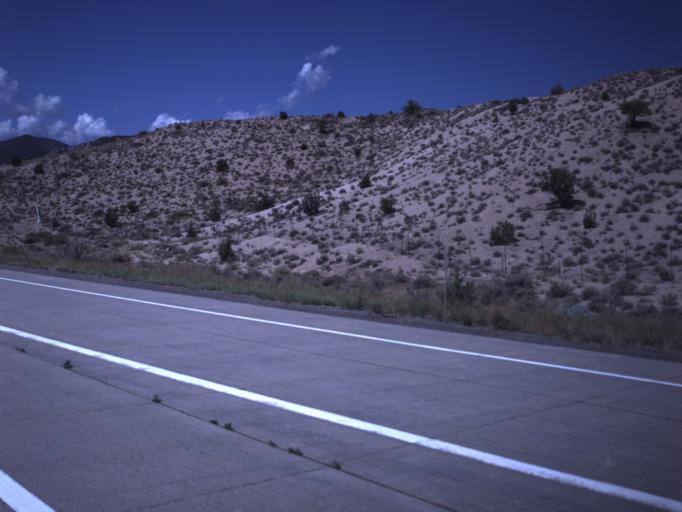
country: US
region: Utah
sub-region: Sevier County
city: Monroe
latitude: 38.5936
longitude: -112.2551
